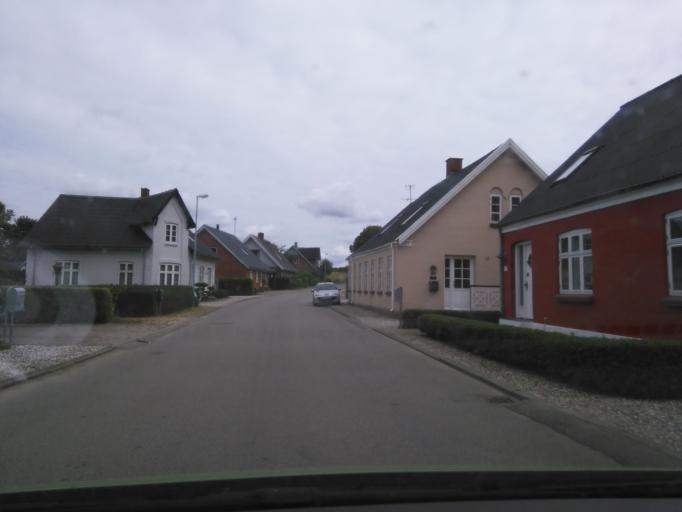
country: DK
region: Central Jutland
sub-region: Arhus Kommune
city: Solbjerg
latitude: 55.9815
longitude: 10.0559
